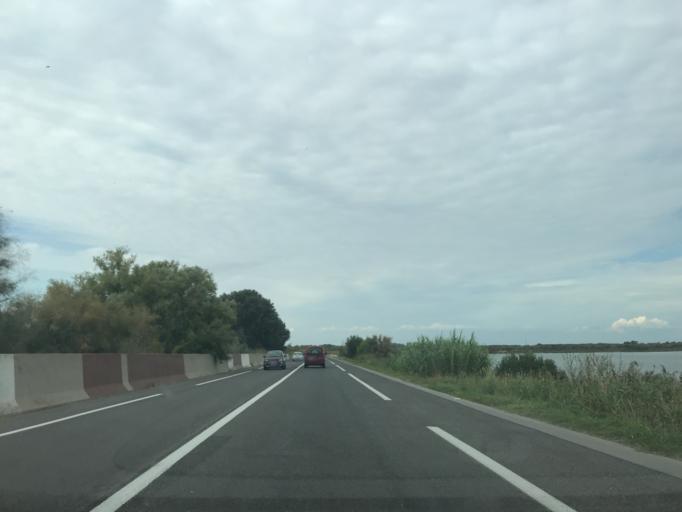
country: FR
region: Languedoc-Roussillon
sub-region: Departement du Gard
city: Le Grau-du-Roi
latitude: 43.5499
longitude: 4.1335
